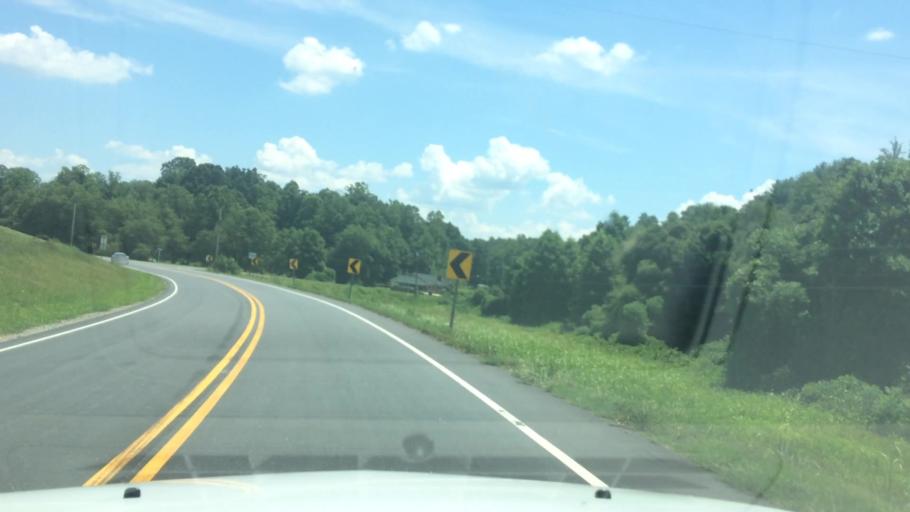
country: US
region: North Carolina
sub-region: Alexander County
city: Taylorsville
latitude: 35.9189
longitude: -81.2542
